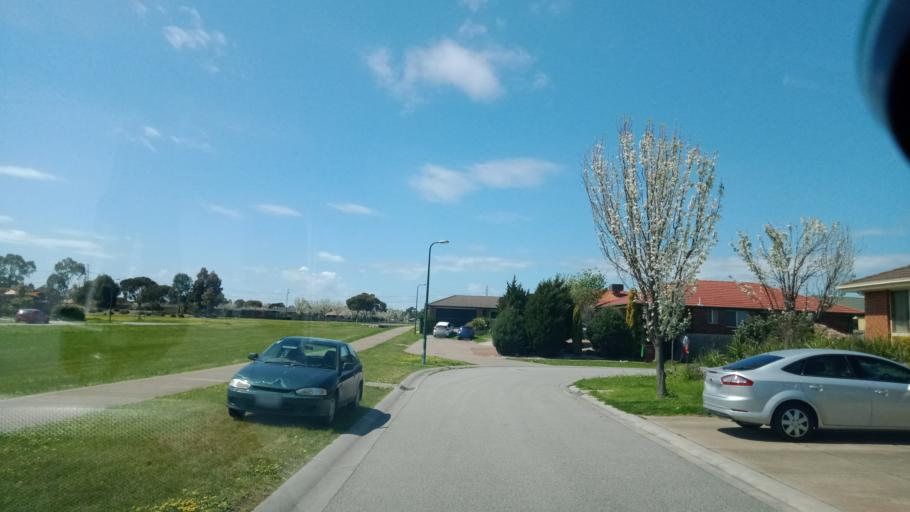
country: AU
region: Victoria
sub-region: Casey
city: Cranbourne West
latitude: -38.0905
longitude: 145.2578
